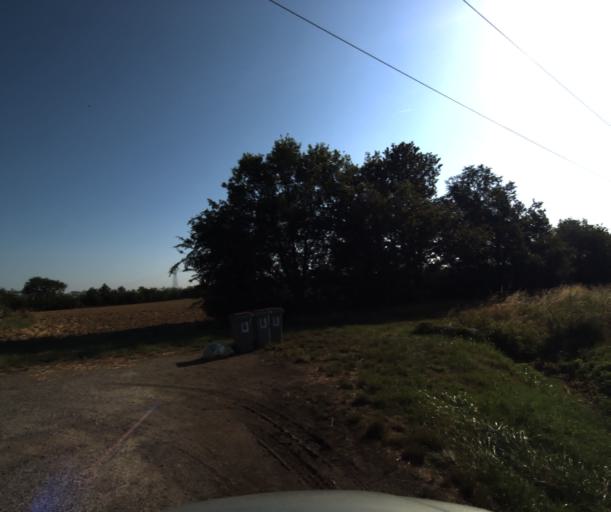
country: FR
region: Midi-Pyrenees
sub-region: Departement de la Haute-Garonne
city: Eaunes
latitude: 43.4374
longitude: 1.3706
